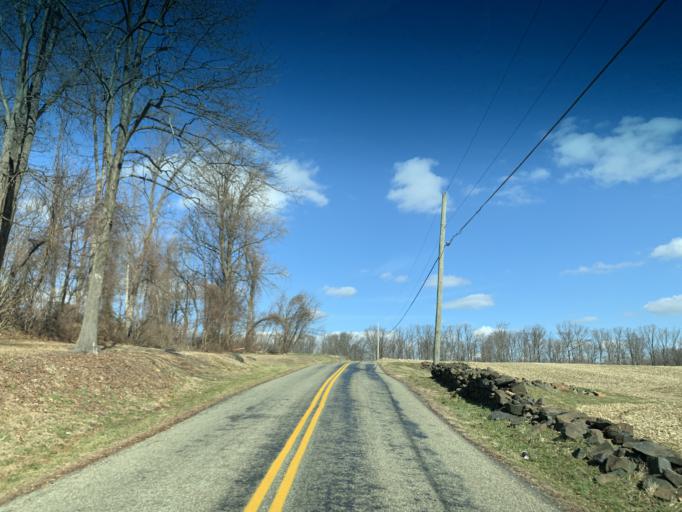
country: US
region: Maryland
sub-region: Harford County
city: Aberdeen
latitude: 39.5412
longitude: -76.2121
